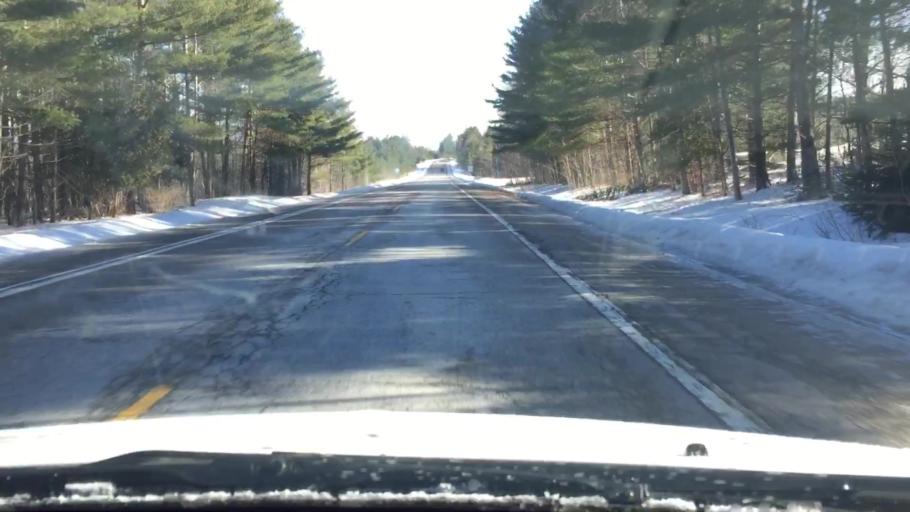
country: US
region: Michigan
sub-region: Charlevoix County
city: East Jordan
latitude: 45.0973
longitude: -85.1066
